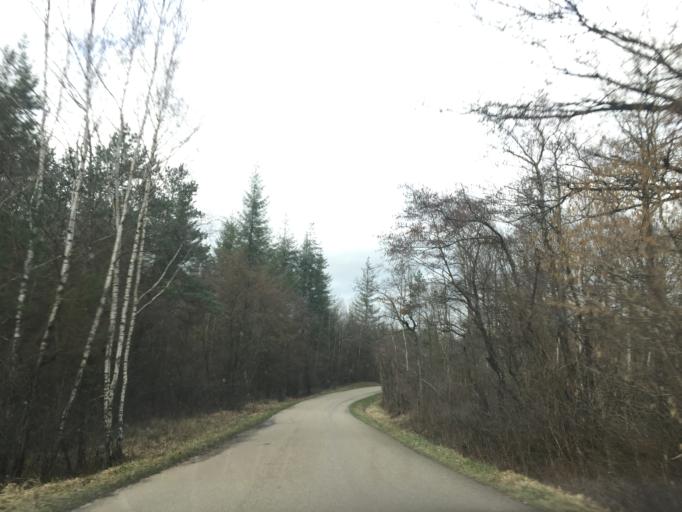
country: BE
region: Wallonia
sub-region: Province du Luxembourg
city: Durbuy
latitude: 50.3194
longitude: 5.4888
